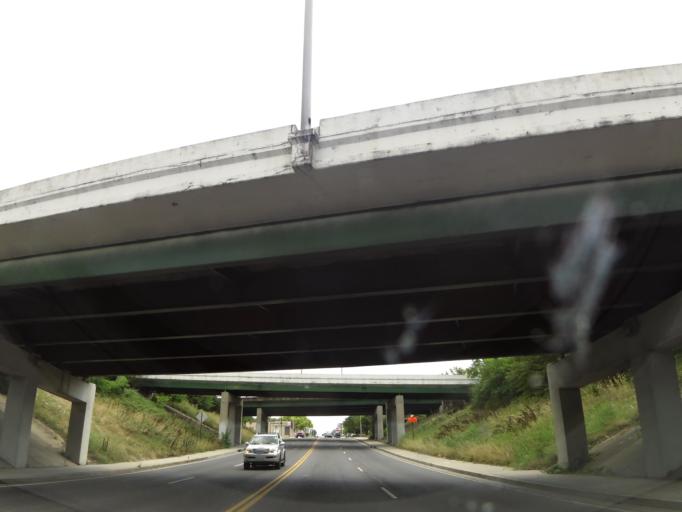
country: US
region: Tennessee
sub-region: Davidson County
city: Nashville
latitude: 36.1490
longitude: -86.7792
